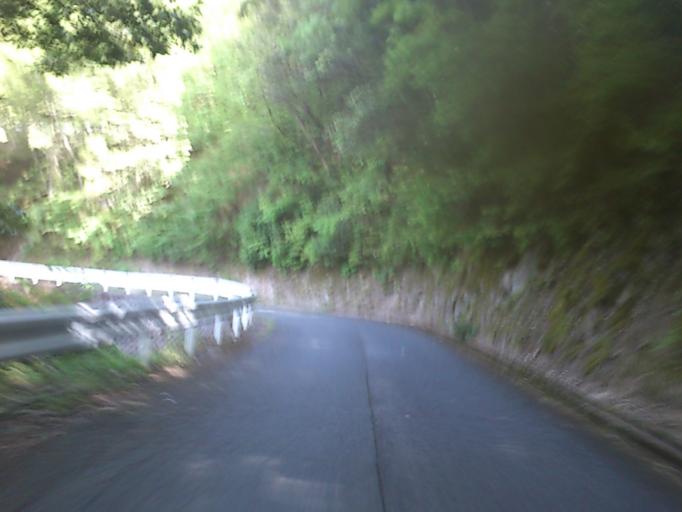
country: JP
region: Kyoto
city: Miyazu
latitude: 35.5654
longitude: 135.1434
